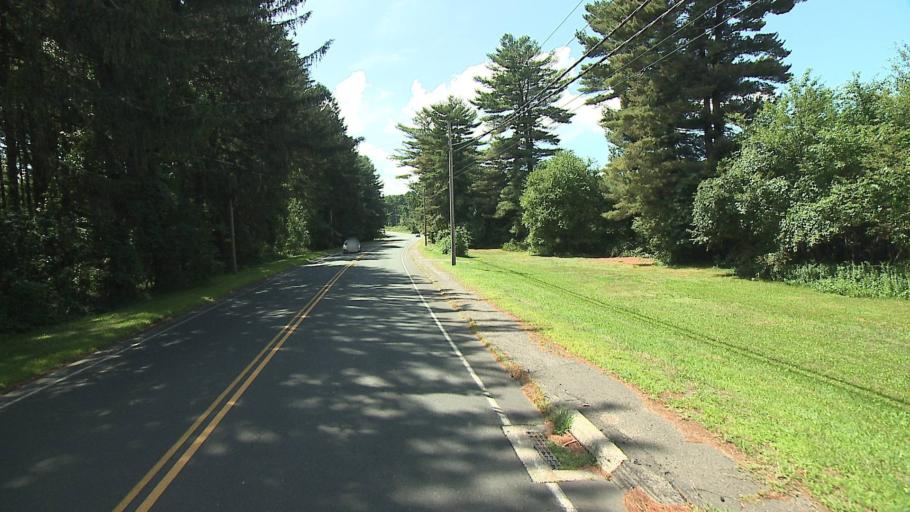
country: US
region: Connecticut
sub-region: Fairfield County
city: Shelton
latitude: 41.3184
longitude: -73.1106
